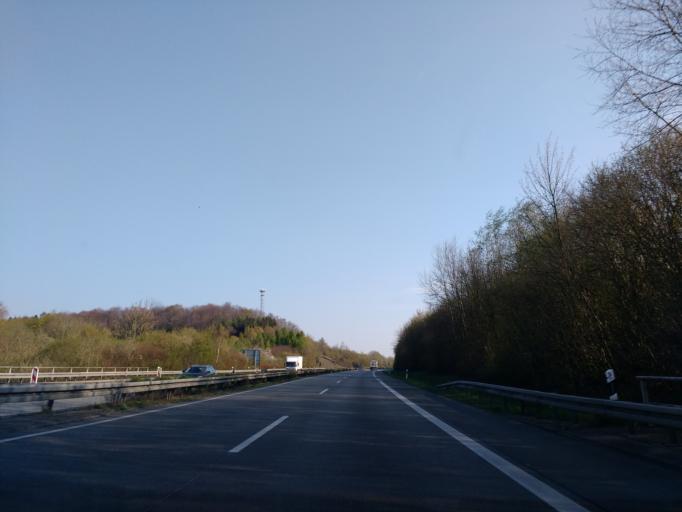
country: DE
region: Lower Saxony
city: Bissendorf
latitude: 52.2001
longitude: 8.1414
